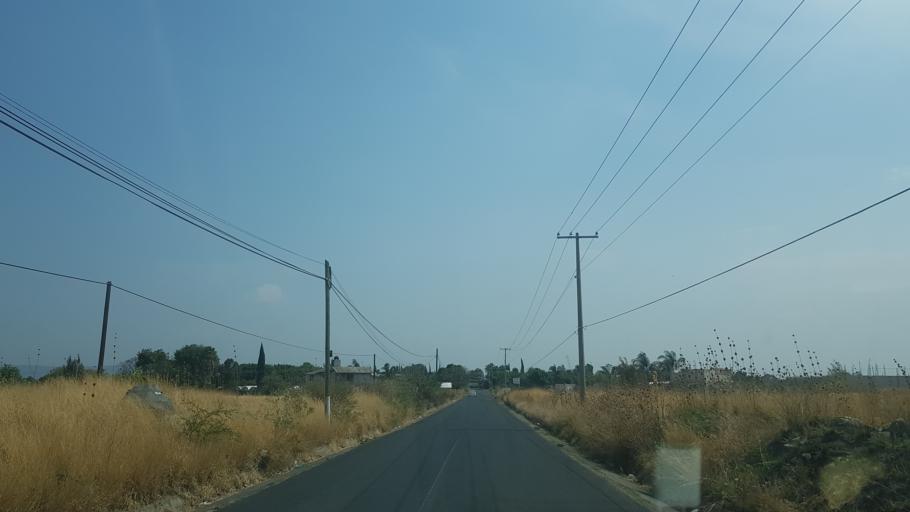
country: MX
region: Puebla
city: Atlixco
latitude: 18.9297
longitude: -98.4543
